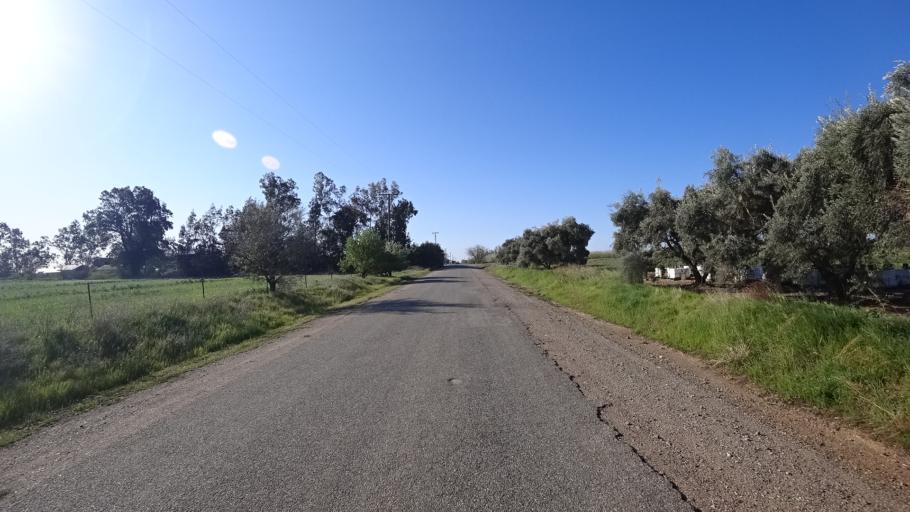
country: US
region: California
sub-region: Glenn County
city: Orland
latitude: 39.7668
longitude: -122.1227
